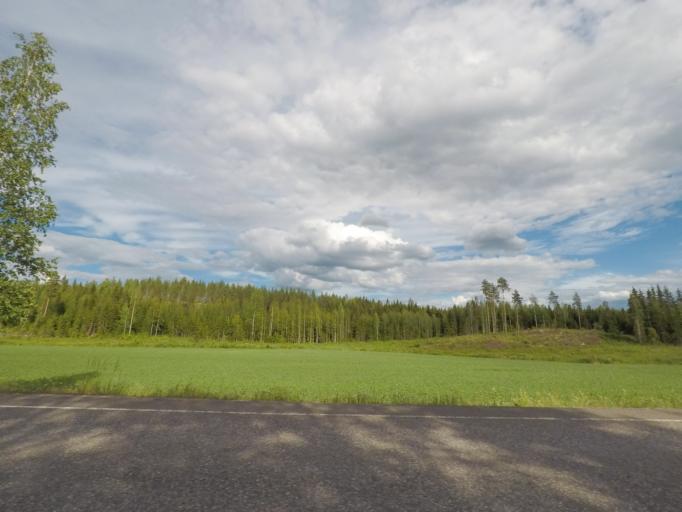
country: FI
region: Paijanne Tavastia
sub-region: Lahti
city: Hollola
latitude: 60.8393
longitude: 25.4938
